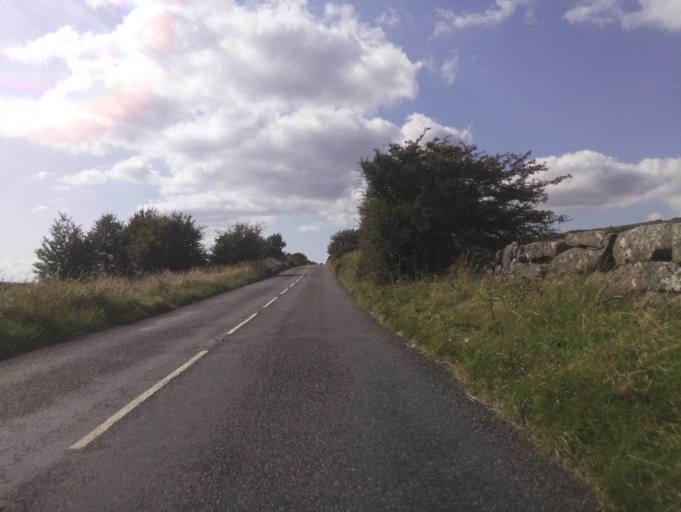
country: GB
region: England
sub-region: Devon
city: Buckfastleigh
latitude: 50.5470
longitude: -3.8944
